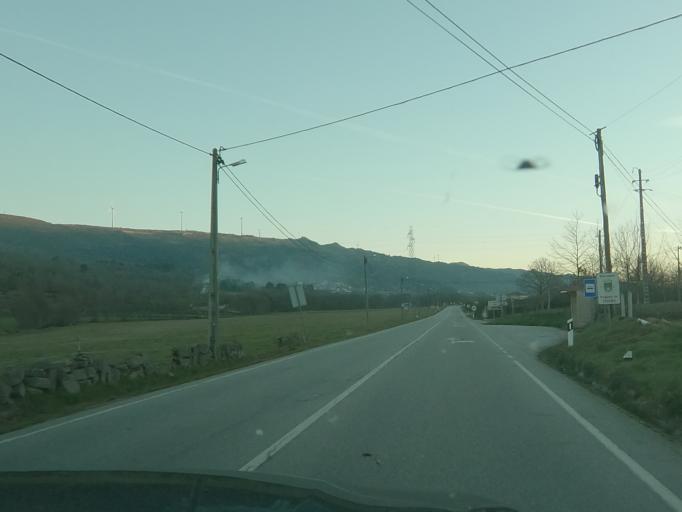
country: PT
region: Vila Real
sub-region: Vila Pouca de Aguiar
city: Vila Pouca de Aguiar
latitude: 41.4637
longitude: -7.6653
